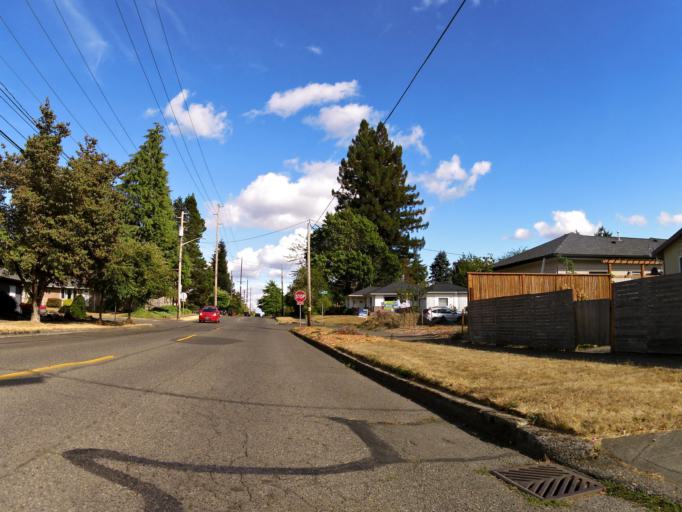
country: US
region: Washington
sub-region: Thurston County
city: Olympia
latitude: 47.0444
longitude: -122.9243
